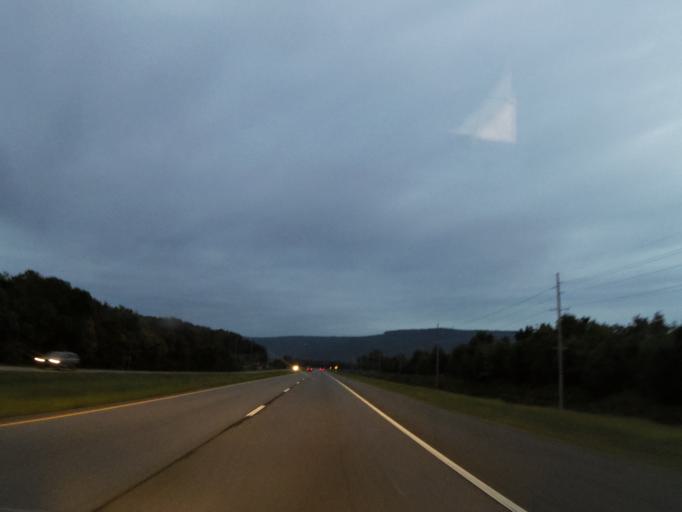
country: US
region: Alabama
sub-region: Madison County
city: Owens Cross Roads
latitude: 34.7087
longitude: -86.3990
